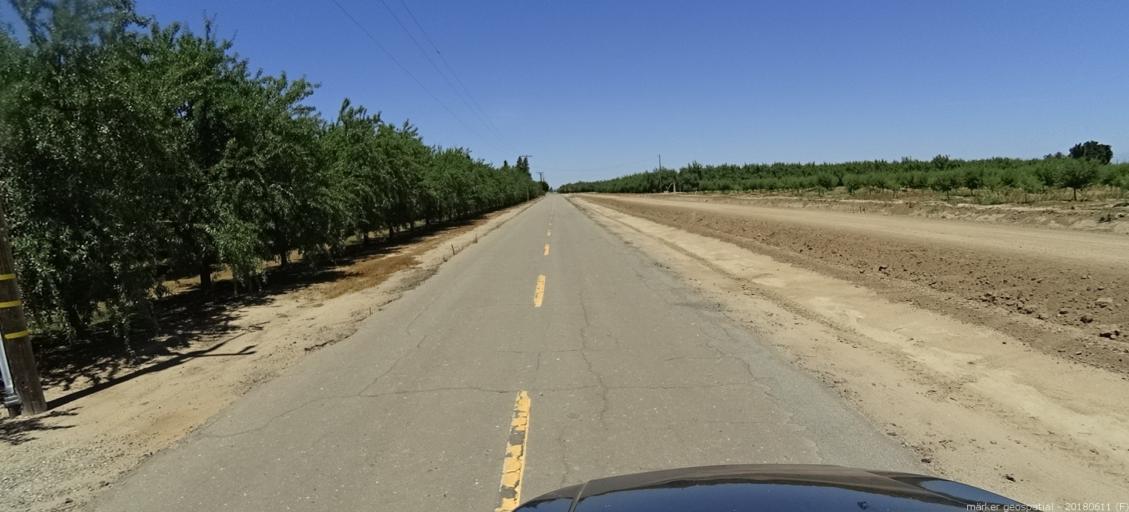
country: US
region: California
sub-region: Madera County
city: Fairmead
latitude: 37.0370
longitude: -120.1932
